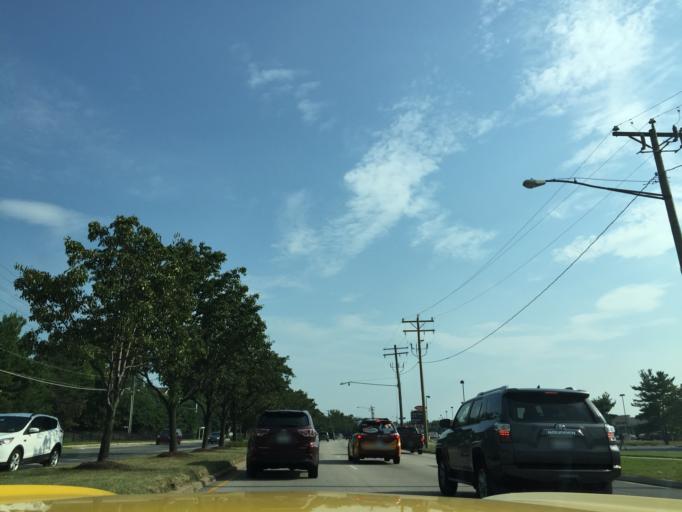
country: US
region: Virginia
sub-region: Fairfax County
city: Hybla Valley
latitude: 38.7473
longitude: -77.0832
